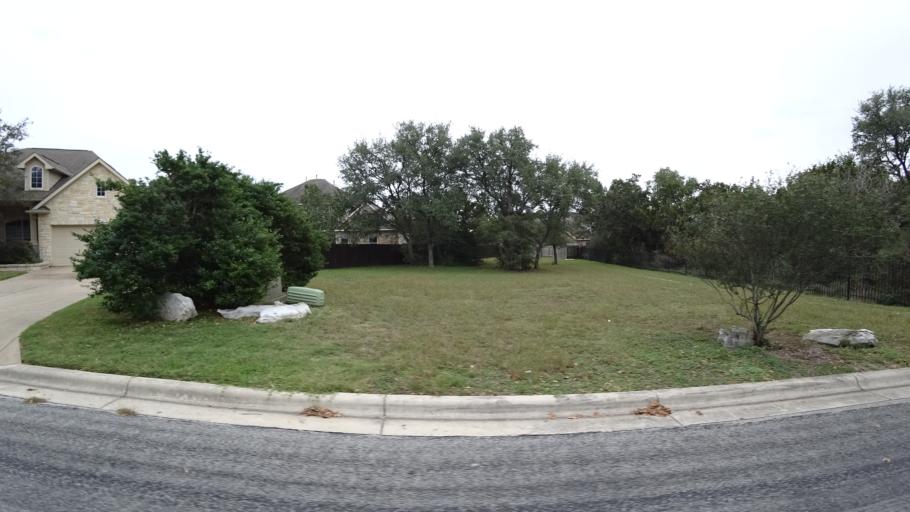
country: US
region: Texas
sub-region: Travis County
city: Shady Hollow
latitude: 30.1851
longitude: -97.9040
